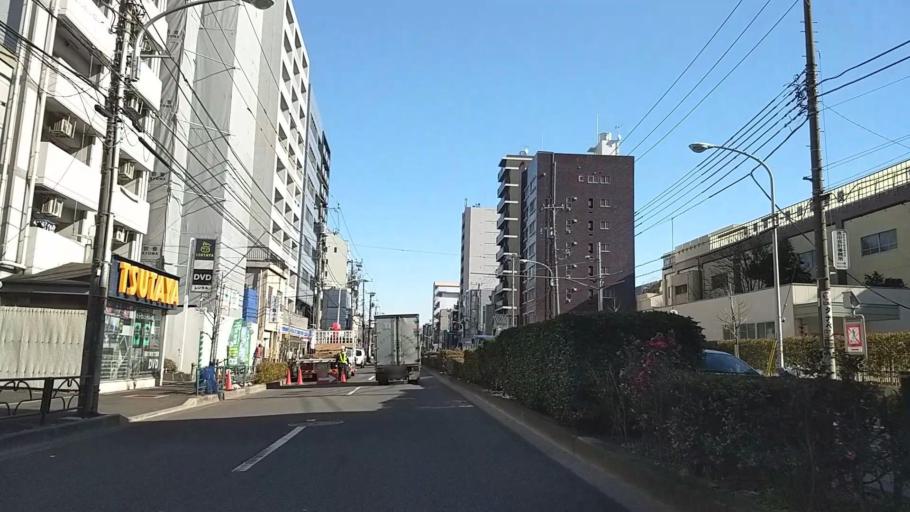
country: JP
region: Tokyo
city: Urayasu
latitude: 35.6888
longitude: 139.8122
